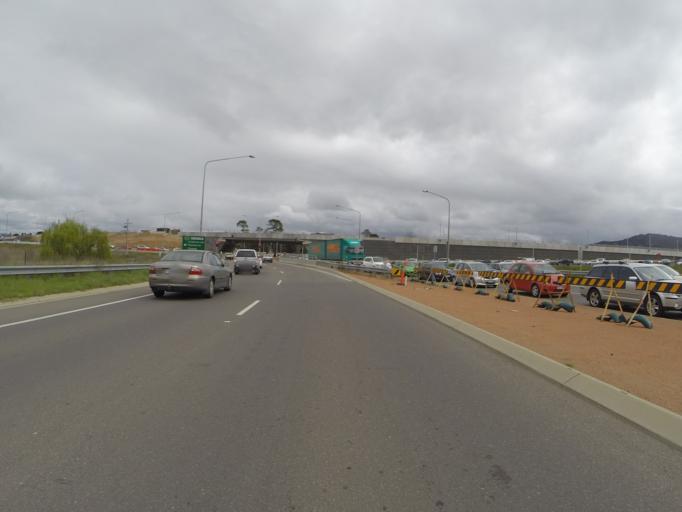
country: AU
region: Australian Capital Territory
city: Forrest
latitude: -35.2988
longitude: 149.1797
